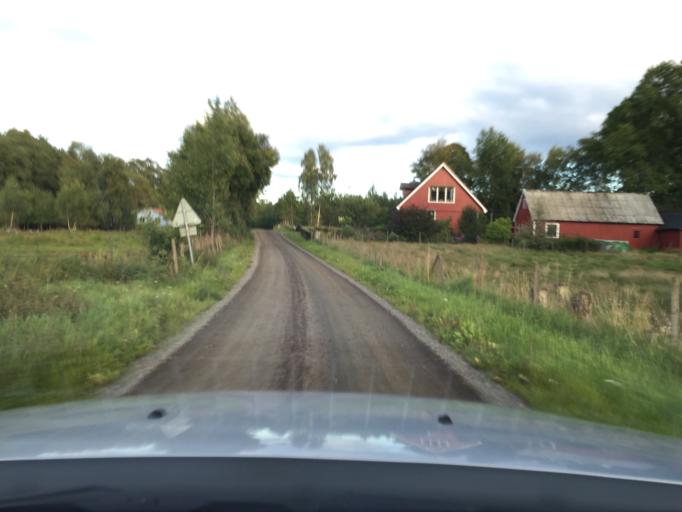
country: SE
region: Skane
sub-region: Hassleholms Kommun
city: Sosdala
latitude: 56.0373
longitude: 13.7101
